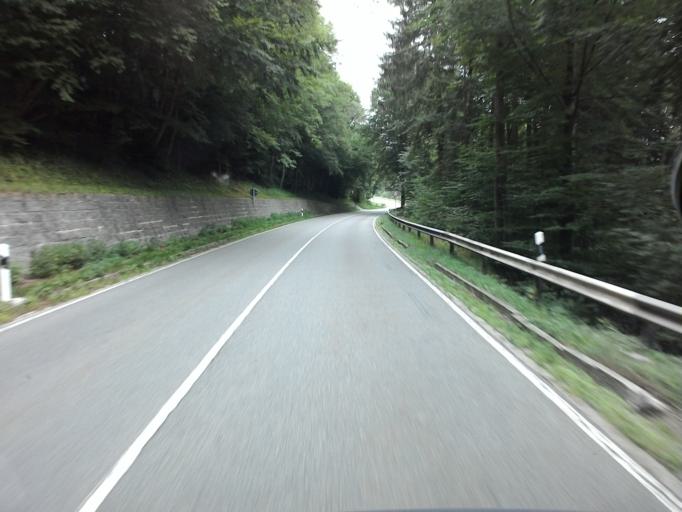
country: DE
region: Bavaria
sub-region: Upper Bavaria
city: Weyarn
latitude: 47.8446
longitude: 11.8111
